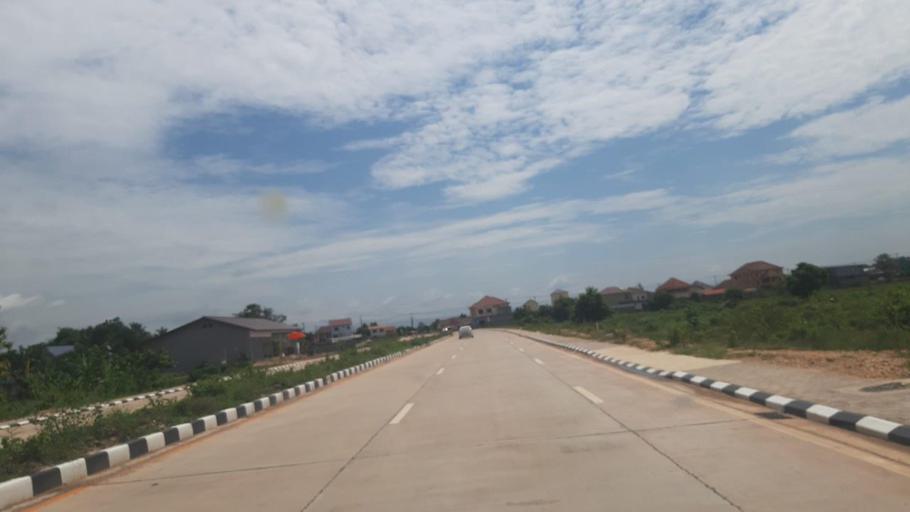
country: LA
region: Vientiane
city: Vientiane
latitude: 18.0371
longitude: 102.6131
